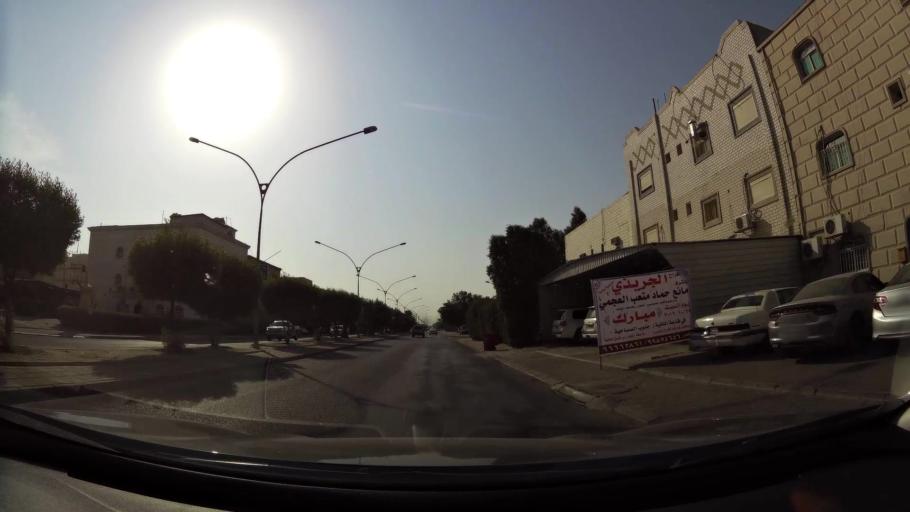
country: KW
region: Al Ahmadi
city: Ar Riqqah
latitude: 29.1607
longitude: 48.0681
